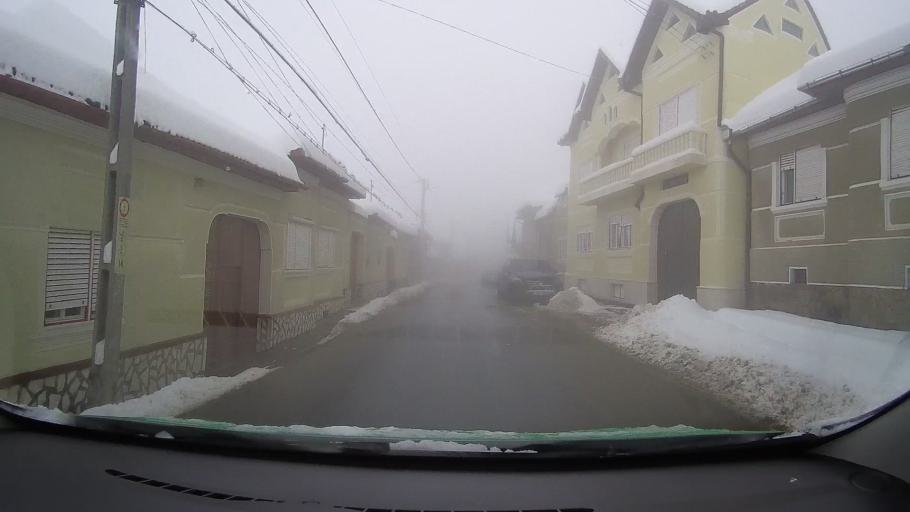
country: RO
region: Sibiu
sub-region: Comuna Poiana Sibiului
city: Poiana Sibiului
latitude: 45.8046
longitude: 23.7223
